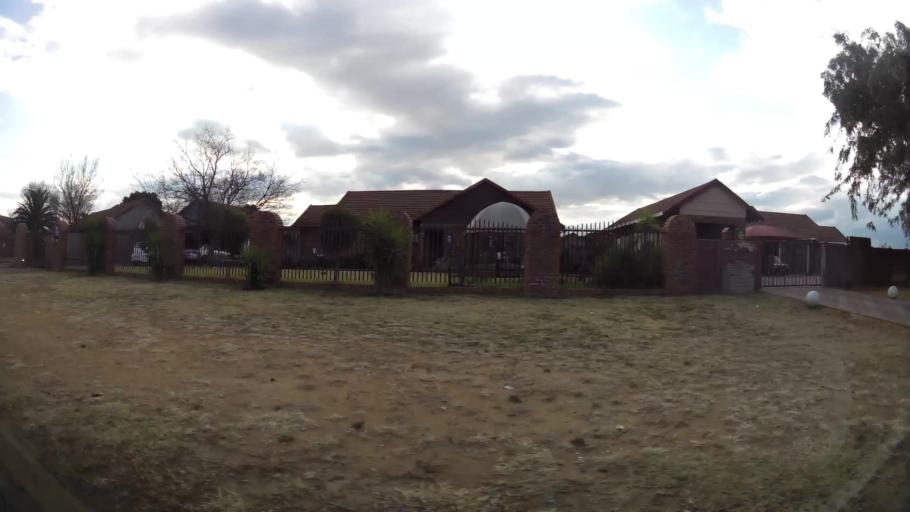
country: ZA
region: Orange Free State
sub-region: Lejweleputswa District Municipality
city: Welkom
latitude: -27.9985
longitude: 26.7413
